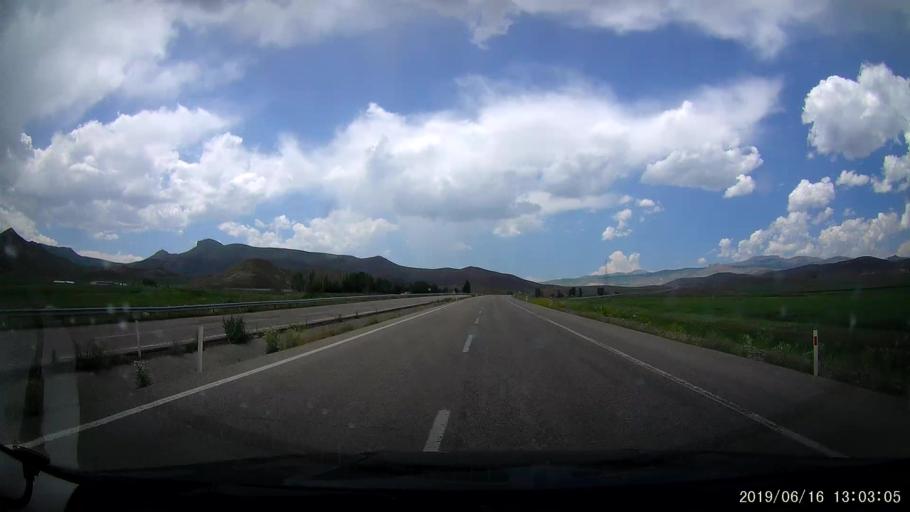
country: TR
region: Agri
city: Sulucem
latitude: 39.5785
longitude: 43.7989
